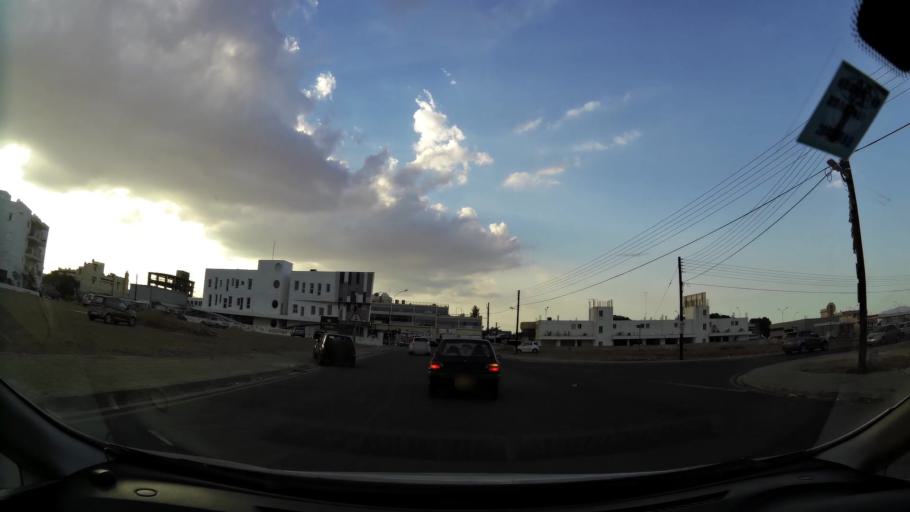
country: CY
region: Lefkosia
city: Tseri
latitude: 35.1223
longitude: 33.3216
